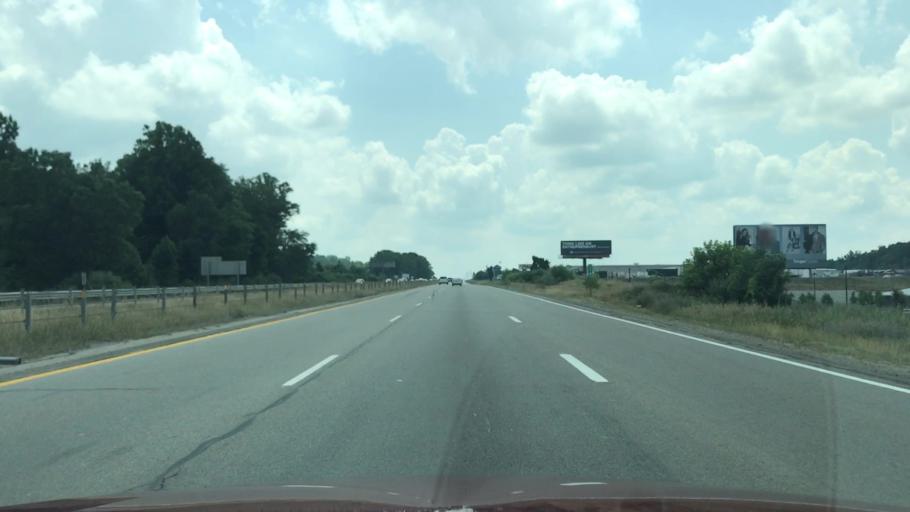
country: US
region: Michigan
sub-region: Kent County
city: Cutlerville
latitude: 42.8099
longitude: -85.6690
